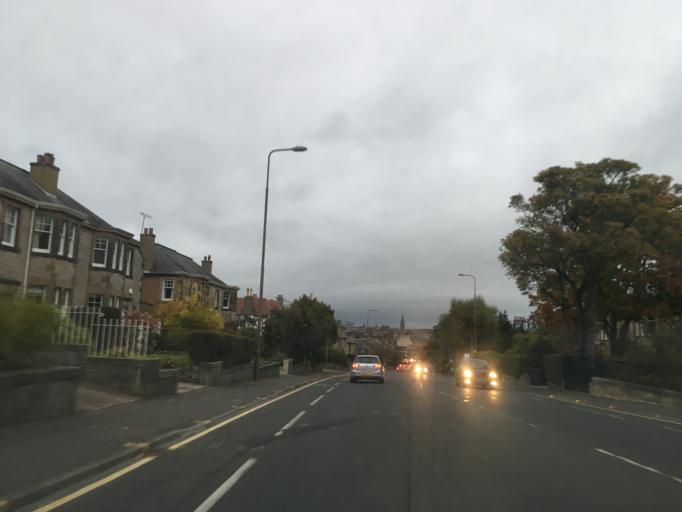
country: GB
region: Scotland
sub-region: Edinburgh
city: Edinburgh
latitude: 55.9260
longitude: -3.1735
